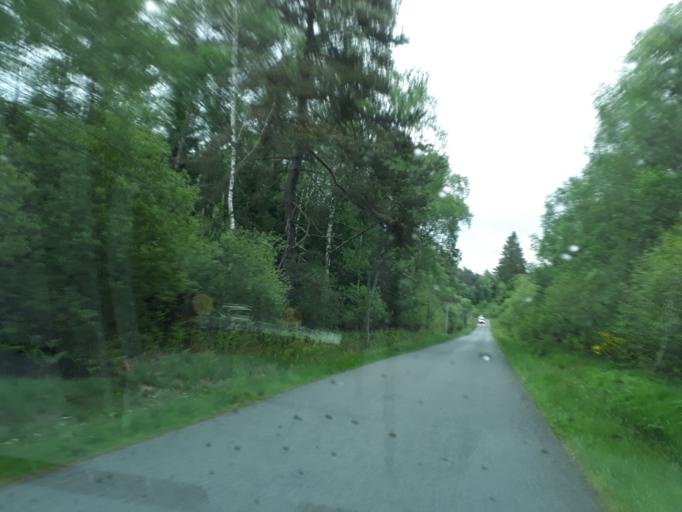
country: FR
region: Limousin
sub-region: Departement de la Haute-Vienne
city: Peyrat-le-Chateau
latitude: 45.8295
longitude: 1.8425
